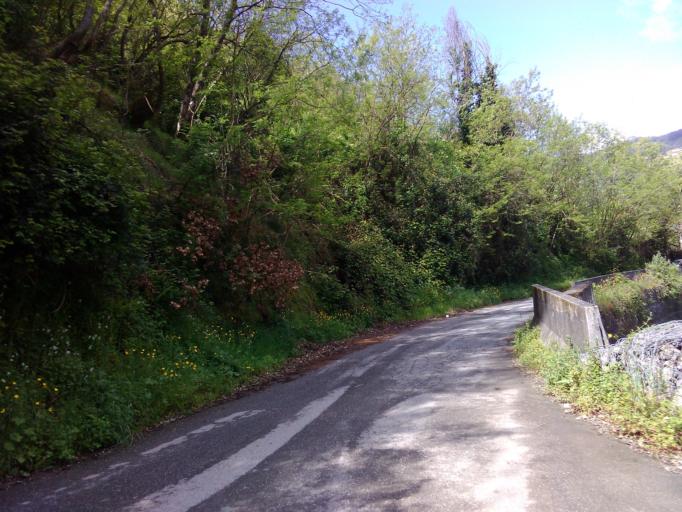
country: IT
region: Tuscany
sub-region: Provincia di Massa-Carrara
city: Carrara
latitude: 44.0668
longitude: 10.0896
